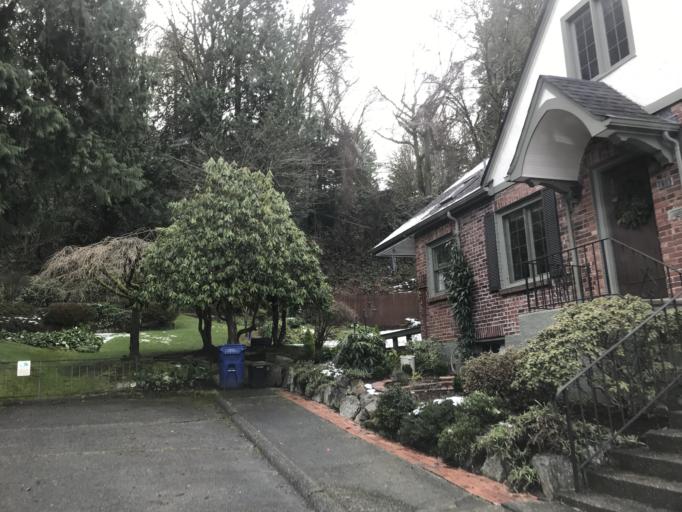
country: US
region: Washington
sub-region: King County
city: Seattle
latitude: 47.6368
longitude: -122.3066
